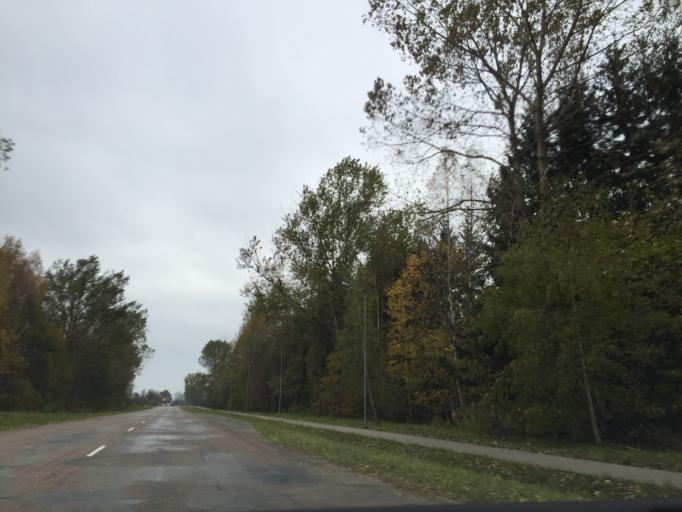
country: LV
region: Marupe
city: Marupe
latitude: 56.8496
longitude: 24.0507
